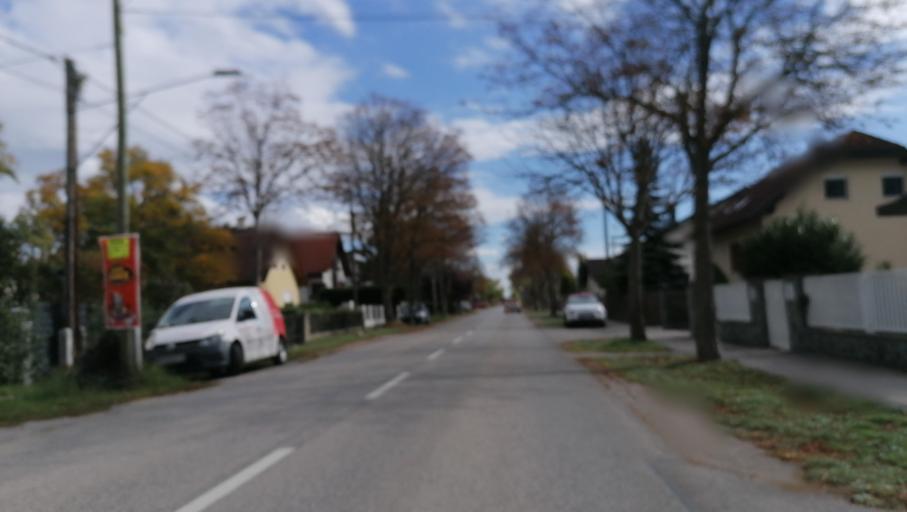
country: AT
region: Lower Austria
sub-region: Politischer Bezirk Baden
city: Teesdorf
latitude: 47.9796
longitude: 16.2747
